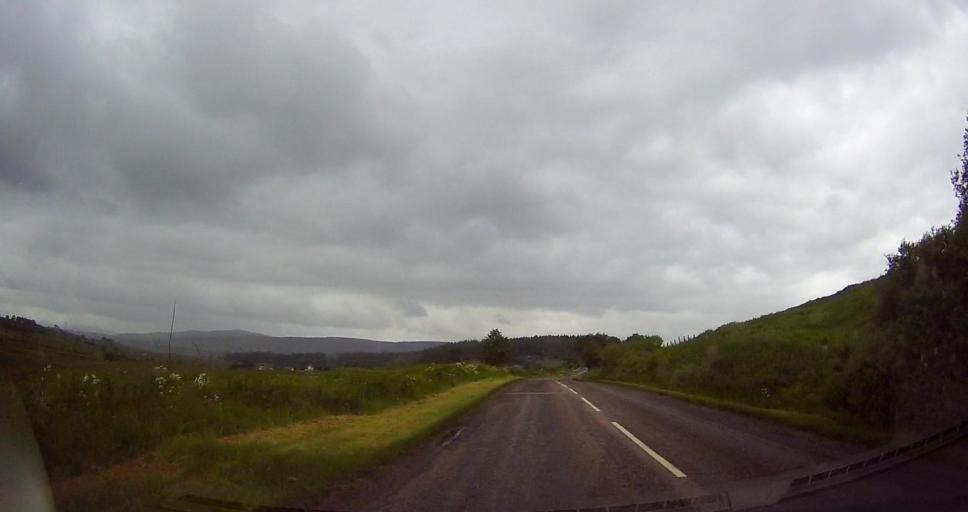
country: GB
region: Scotland
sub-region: Highland
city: Alness
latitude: 58.0183
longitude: -4.3618
